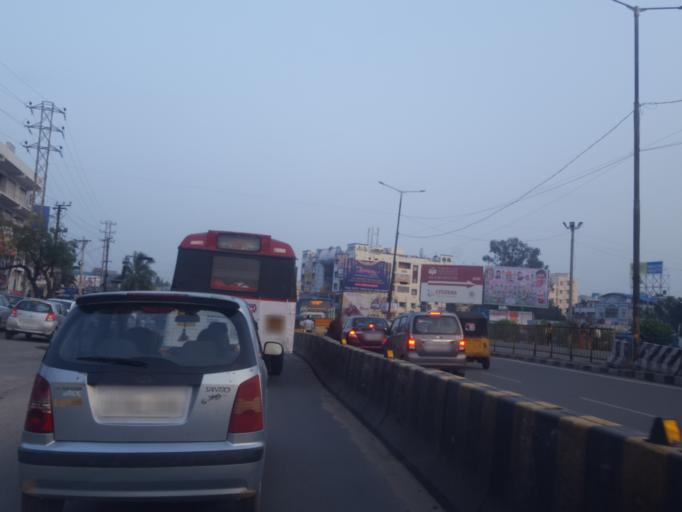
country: IN
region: Telangana
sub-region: Medak
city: Serilingampalle
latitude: 17.4956
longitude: 78.3161
